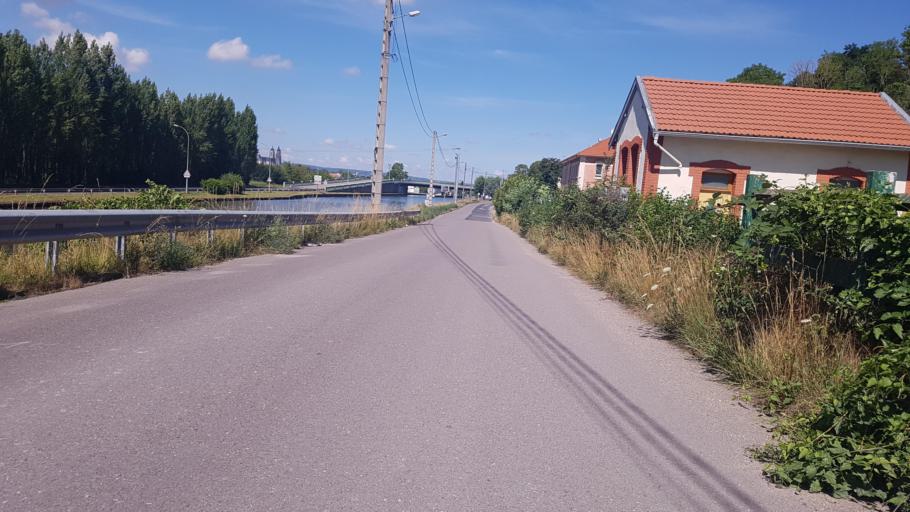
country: FR
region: Lorraine
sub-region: Departement de Meurthe-et-Moselle
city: Varangeville
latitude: 48.6313
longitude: 6.3306
